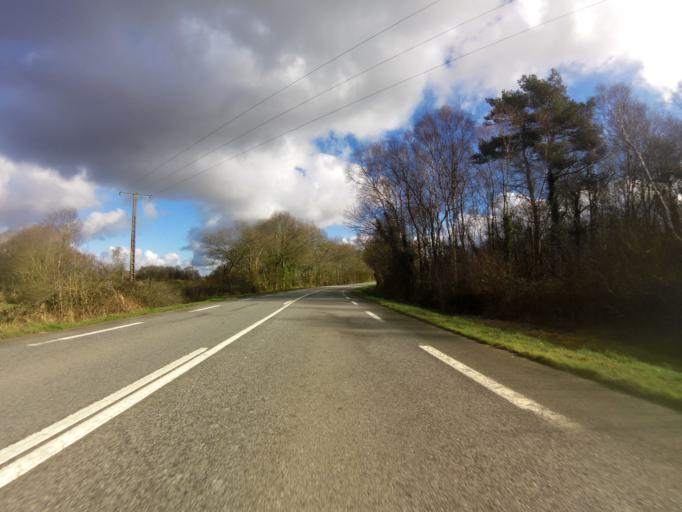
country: FR
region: Brittany
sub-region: Departement du Morbihan
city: Plouray
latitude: 48.1444
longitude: -3.4378
